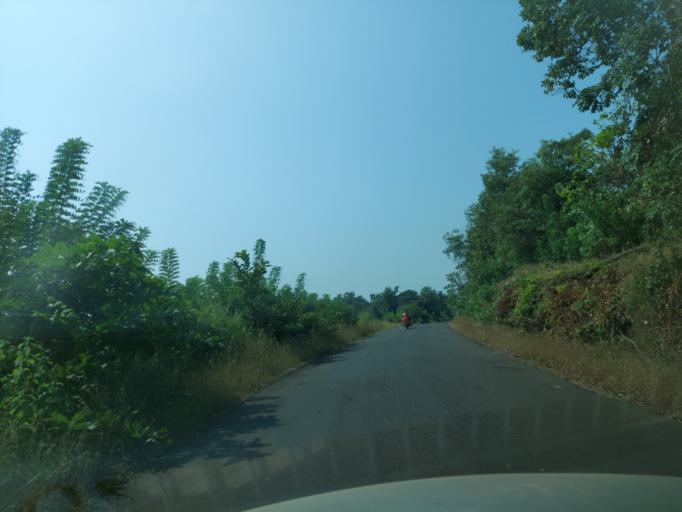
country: IN
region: Maharashtra
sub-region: Sindhudurg
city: Kudal
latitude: 15.9838
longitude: 73.6684
